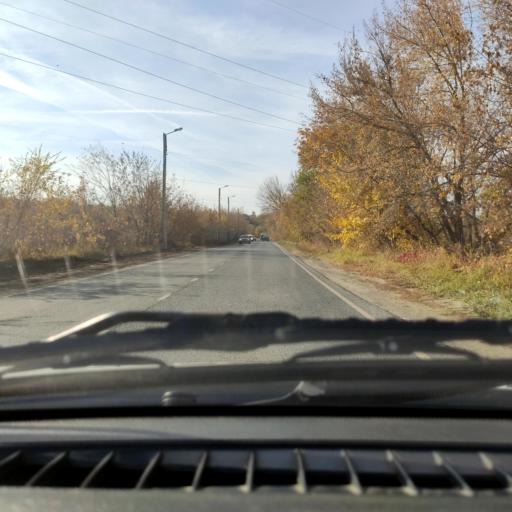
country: RU
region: Samara
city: Zhigulevsk
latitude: 53.5148
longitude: 49.4715
